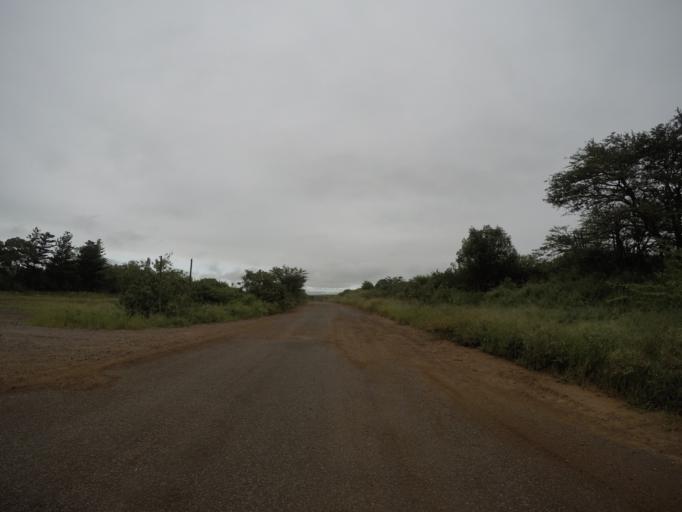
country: ZA
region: KwaZulu-Natal
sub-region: uThungulu District Municipality
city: Empangeni
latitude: -28.6596
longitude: 31.7853
